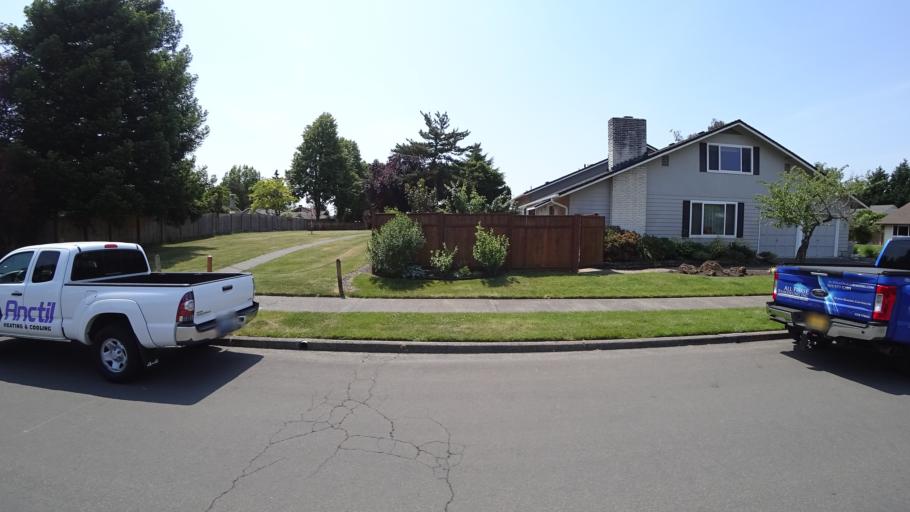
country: US
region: Oregon
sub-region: Washington County
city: Oak Hills
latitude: 45.5414
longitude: -122.8300
